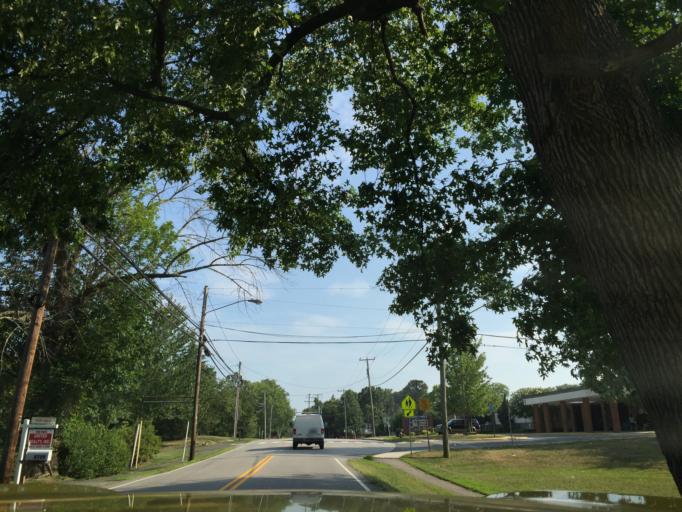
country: US
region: Virginia
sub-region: Fairfax County
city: Mount Vernon
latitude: 38.7212
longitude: -77.0954
